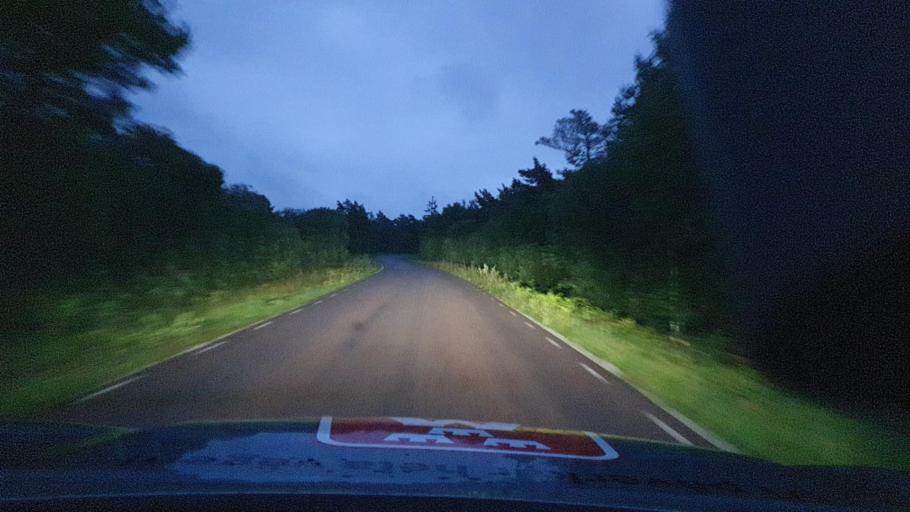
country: SE
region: Gotland
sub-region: Gotland
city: Slite
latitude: 57.7596
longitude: 18.8591
